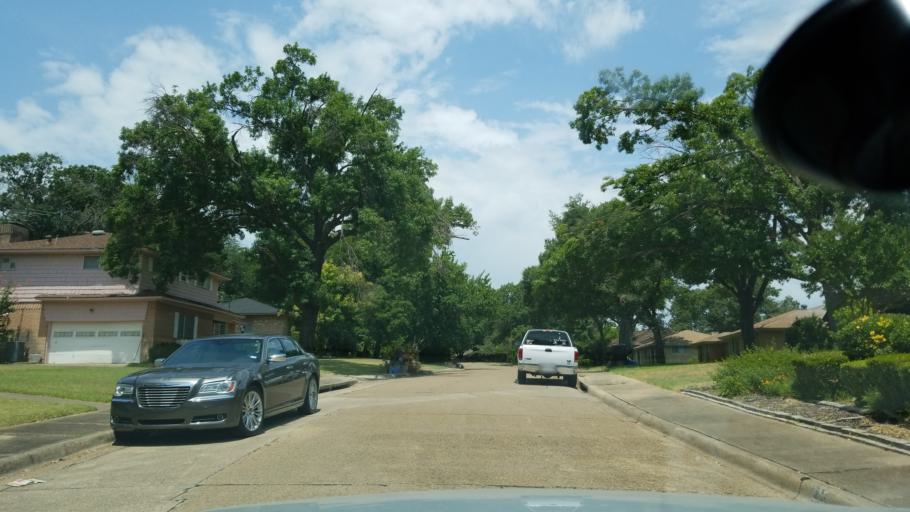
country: US
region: Texas
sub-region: Dallas County
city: Duncanville
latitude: 32.6765
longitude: -96.8365
